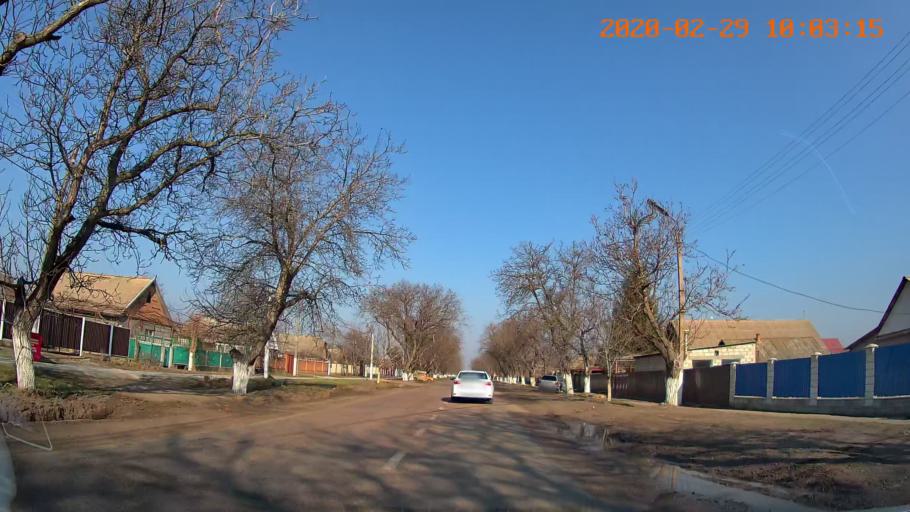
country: MD
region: Causeni
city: Chitcani
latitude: 46.7893
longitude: 29.6810
